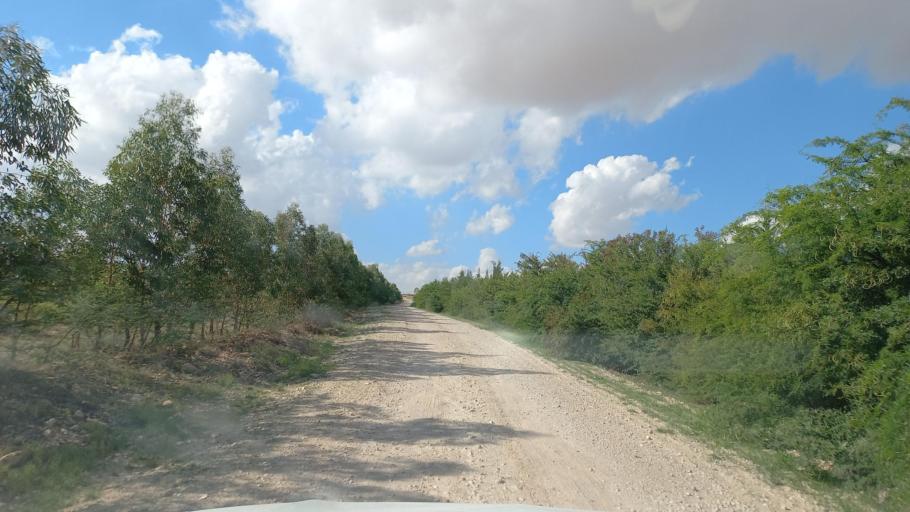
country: TN
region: Al Qasrayn
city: Sbiba
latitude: 35.3388
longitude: 9.0778
